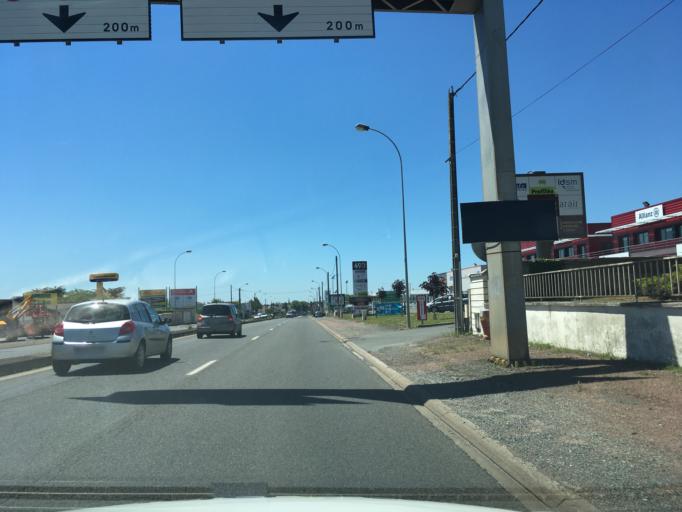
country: FR
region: Poitou-Charentes
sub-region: Departement des Deux-Sevres
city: Niort
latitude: 46.3377
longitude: -0.4184
